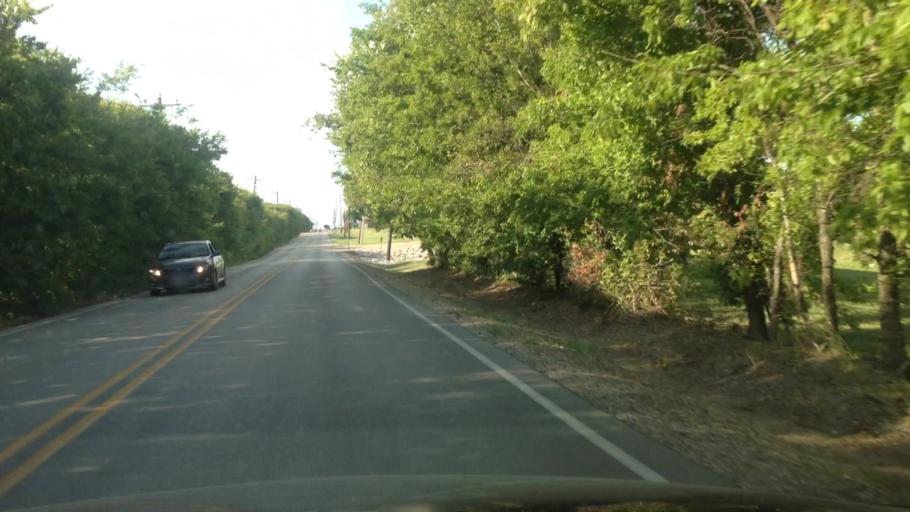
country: US
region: Texas
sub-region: Tarrant County
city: Haslet
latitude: 32.9332
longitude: -97.3920
